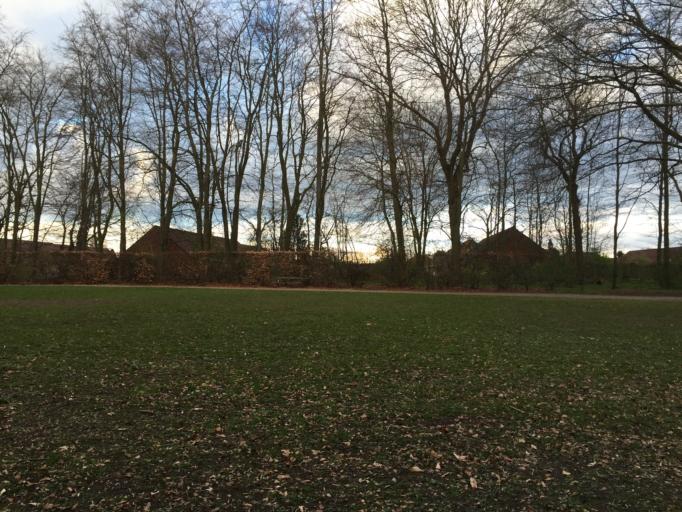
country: DK
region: South Denmark
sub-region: Odense Kommune
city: Odense
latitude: 55.3843
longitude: 10.4082
